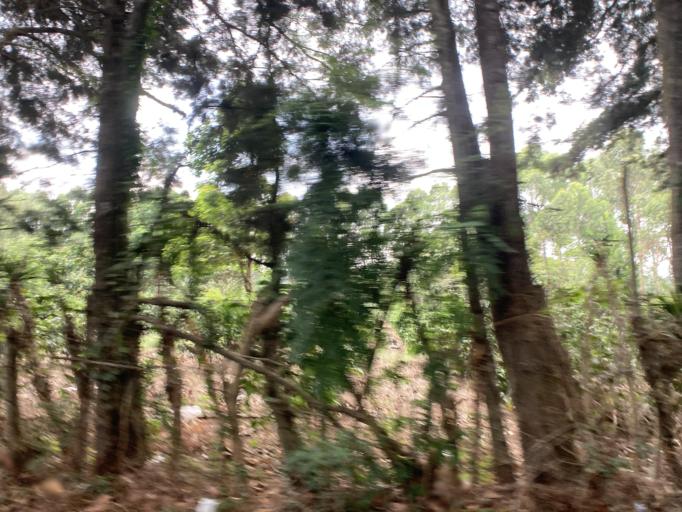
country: GT
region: Guatemala
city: Villa Canales
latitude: 14.4293
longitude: -90.5185
